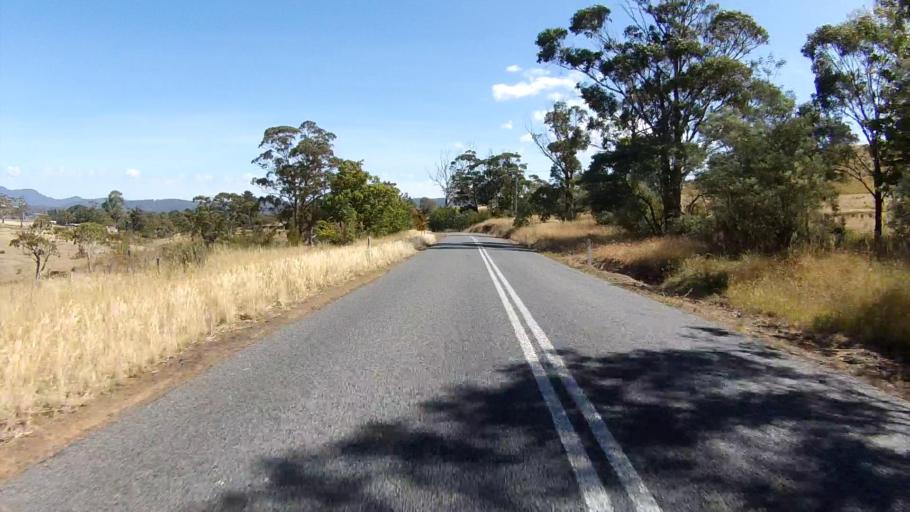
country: AU
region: Tasmania
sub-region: Sorell
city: Sorell
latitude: -42.4922
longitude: 147.9297
